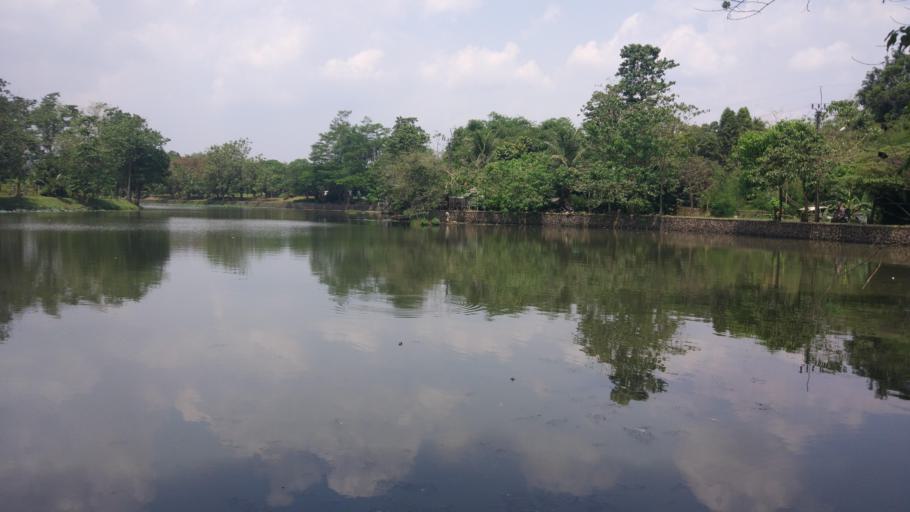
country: ID
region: West Java
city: Ciampea
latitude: -6.5457
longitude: 106.7320
